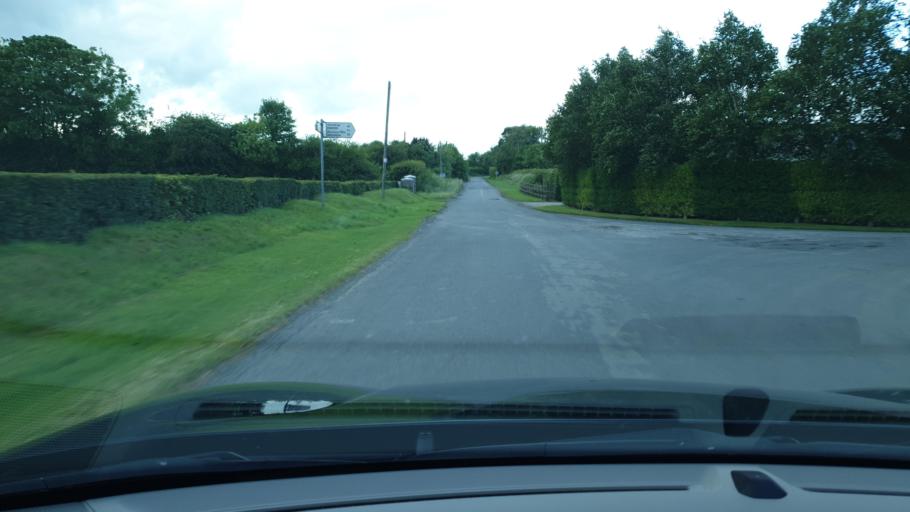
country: IE
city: Kentstown
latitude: 53.5680
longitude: -6.4949
